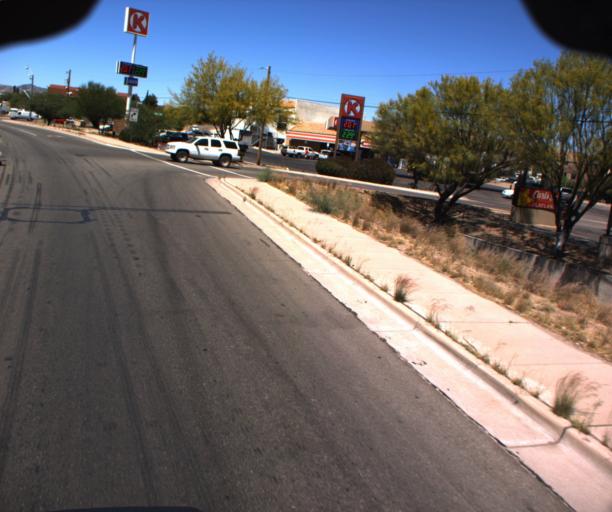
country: US
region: Arizona
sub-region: Santa Cruz County
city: Nogales
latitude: 31.3646
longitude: -110.9474
